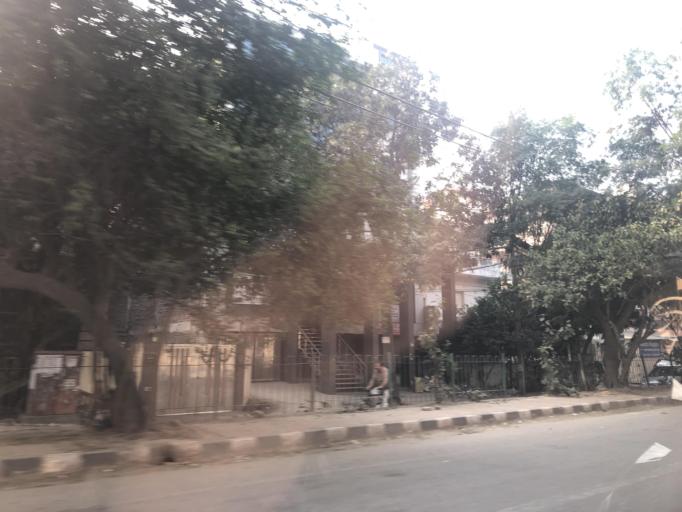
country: IN
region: NCT
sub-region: West Delhi
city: Nangloi Jat
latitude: 28.6790
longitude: 77.0987
